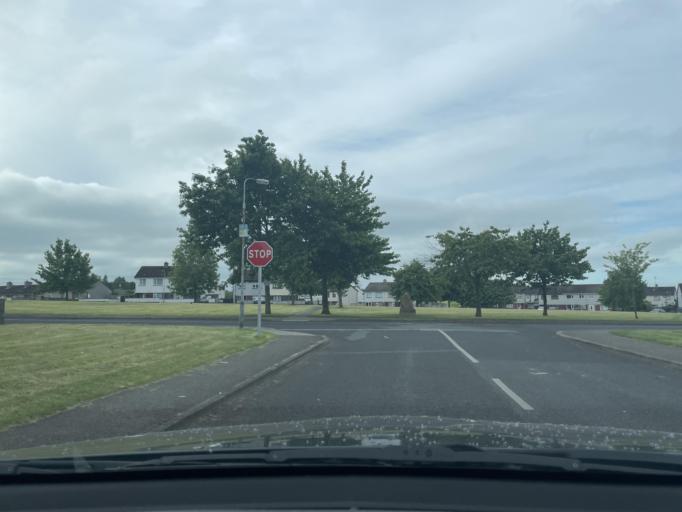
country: IE
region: Leinster
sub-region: County Carlow
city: Bagenalstown
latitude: 52.6982
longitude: -6.9635
